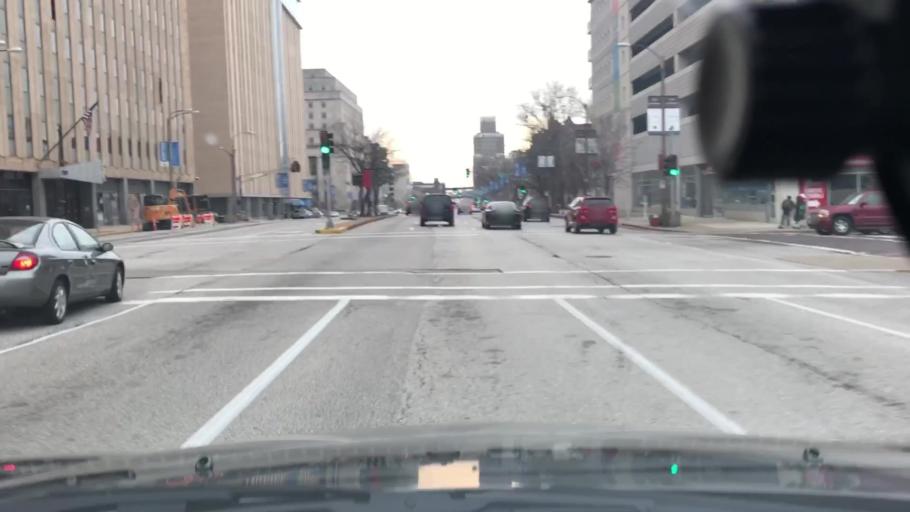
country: US
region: Missouri
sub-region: City of Saint Louis
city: St. Louis
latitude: 38.6299
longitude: -90.1974
